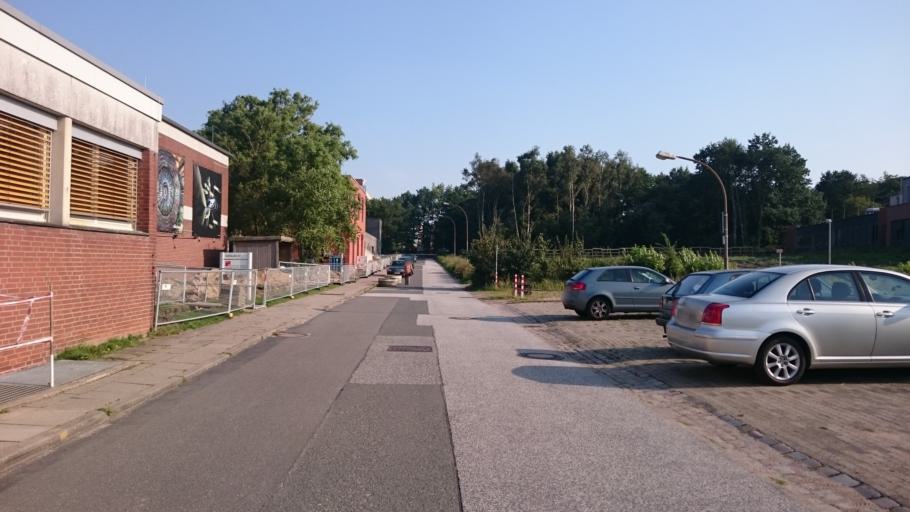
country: DE
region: Hamburg
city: Eidelstedt
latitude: 53.5781
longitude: 9.8853
